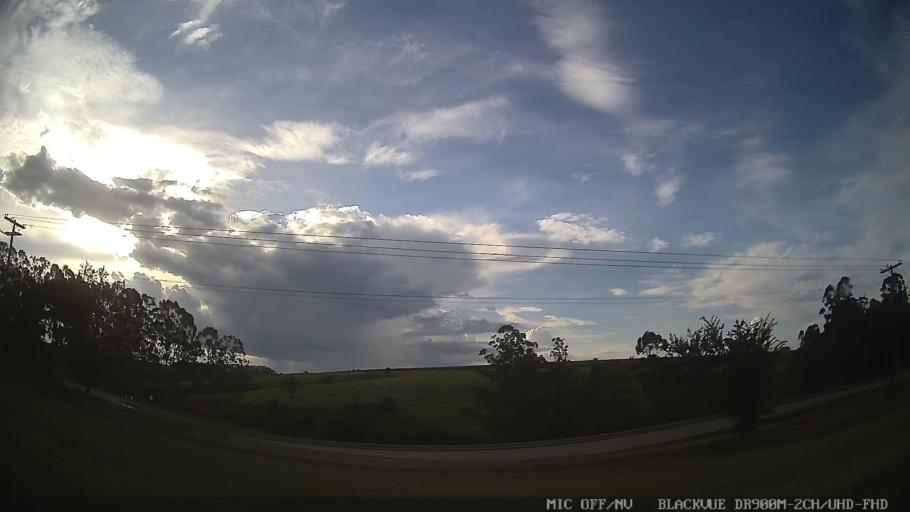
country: BR
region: Sao Paulo
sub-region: Tiete
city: Tiete
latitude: -23.0599
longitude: -47.7233
